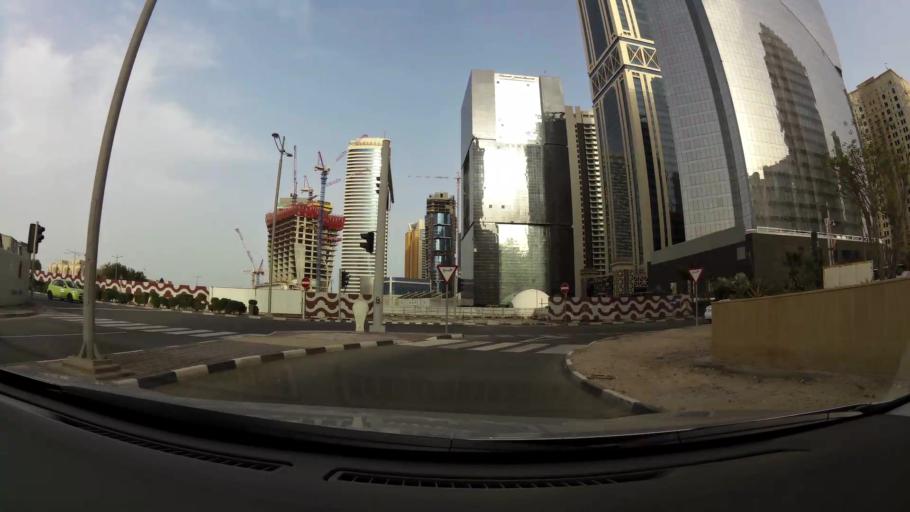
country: QA
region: Baladiyat ad Dawhah
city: Doha
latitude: 25.3297
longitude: 51.5293
